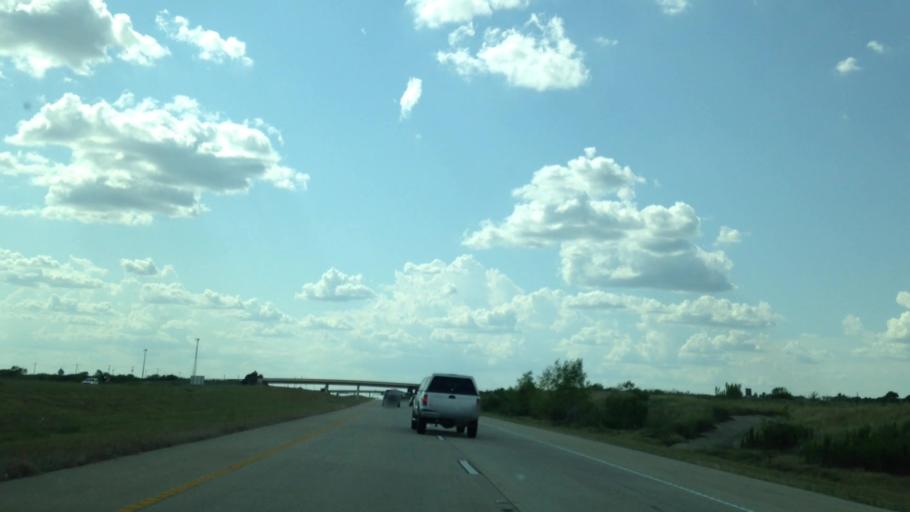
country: US
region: Texas
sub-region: Travis County
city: Onion Creek
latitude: 30.0912
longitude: -97.7496
